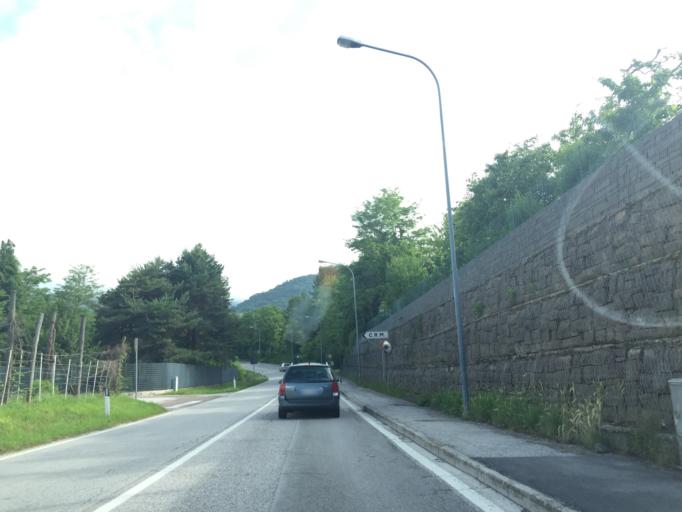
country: IT
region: Trentino-Alto Adige
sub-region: Provincia di Trento
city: Povo
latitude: 46.0580
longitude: 11.1498
